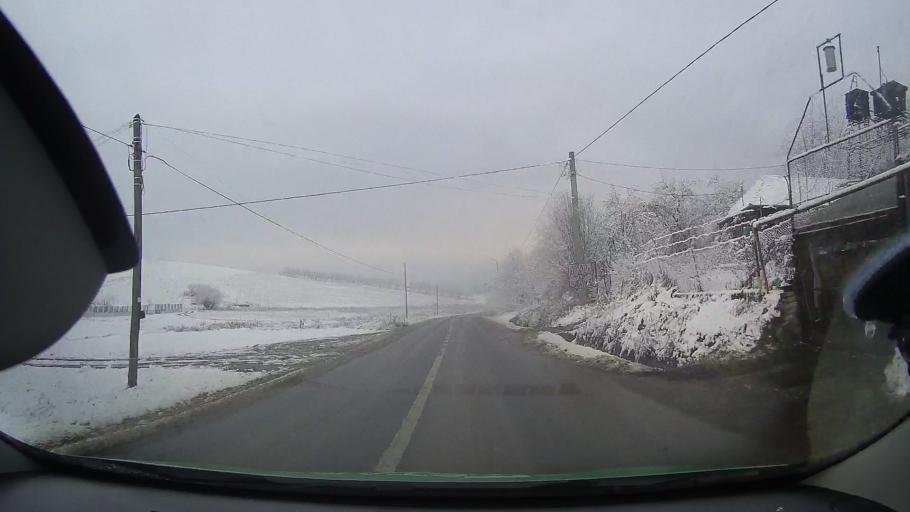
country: RO
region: Mures
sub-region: Comuna Bogata
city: Bogata
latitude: 46.4489
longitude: 24.0864
